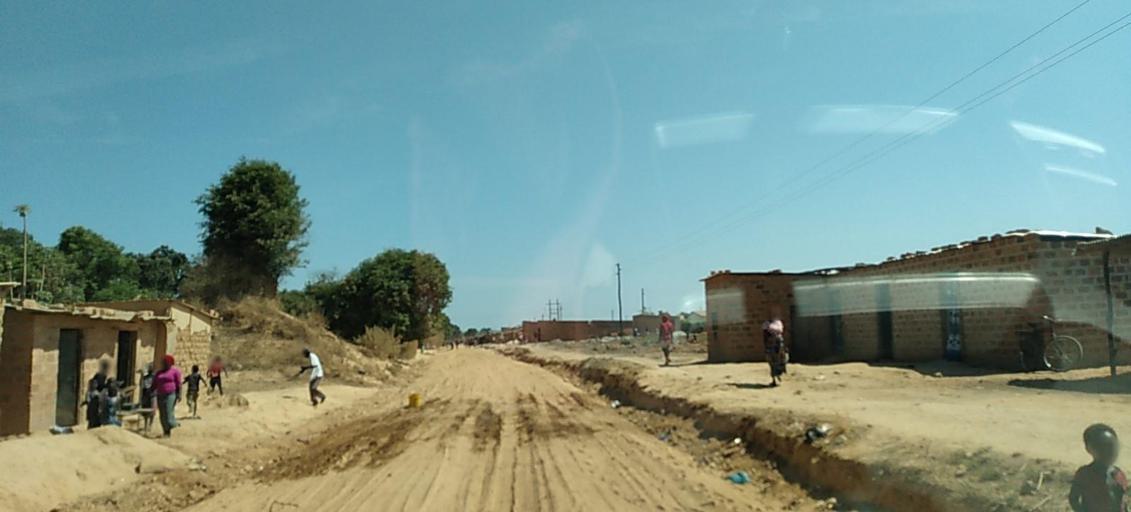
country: ZM
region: Copperbelt
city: Chililabombwe
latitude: -12.3295
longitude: 27.8603
